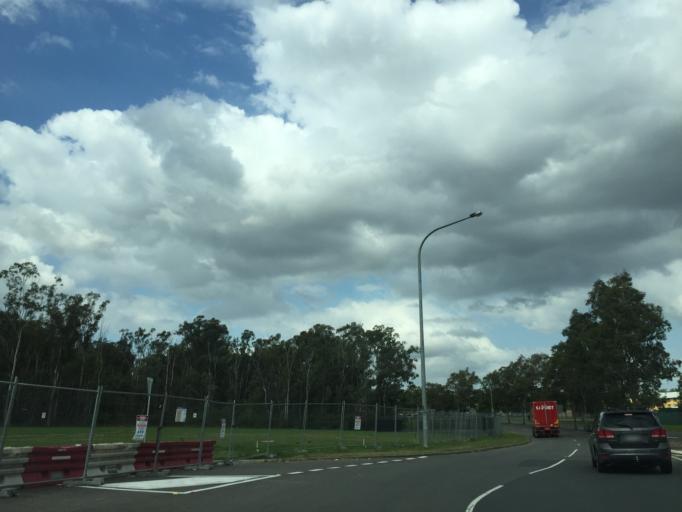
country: AU
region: New South Wales
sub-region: Blacktown
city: Blacktown
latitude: -33.7915
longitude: 150.8944
